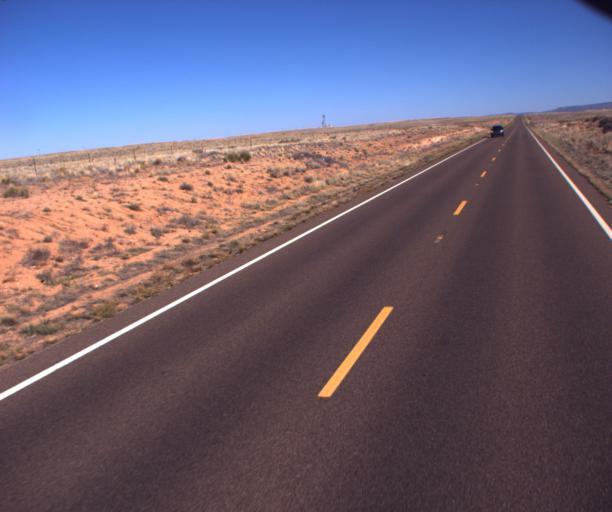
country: US
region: Arizona
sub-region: Navajo County
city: Winslow
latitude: 35.1312
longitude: -110.4957
